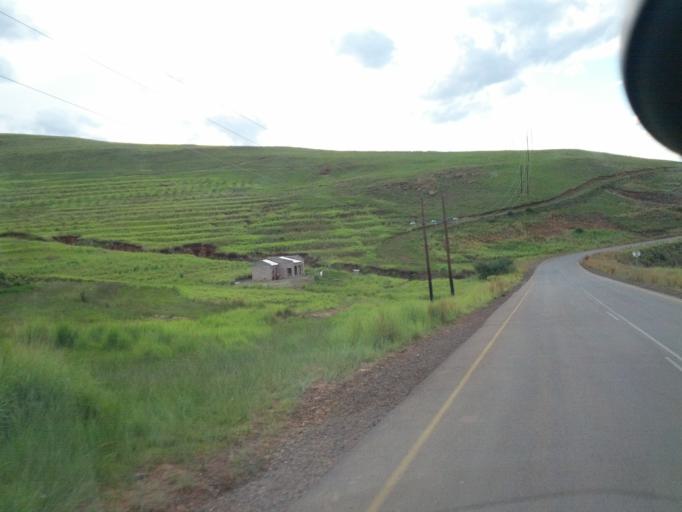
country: LS
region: Qacha's Nek
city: Qacha's Nek
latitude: -30.0904
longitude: 28.6413
